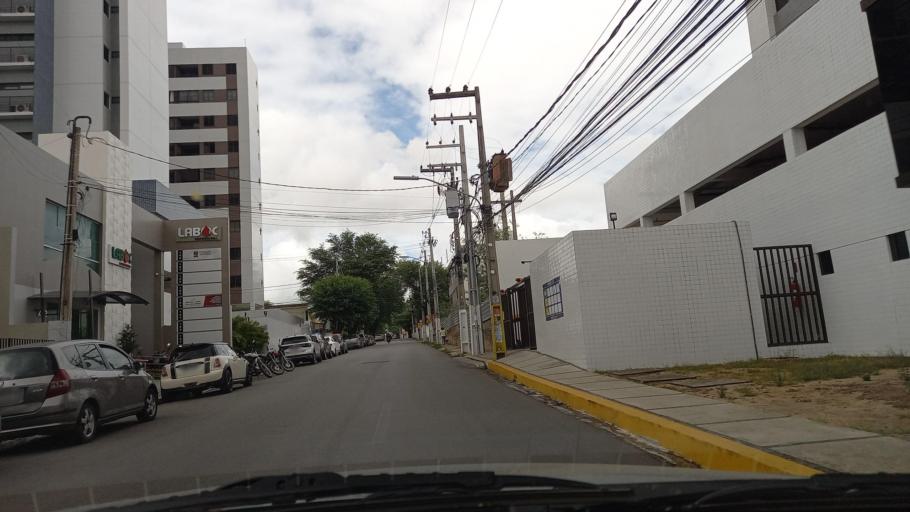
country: BR
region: Pernambuco
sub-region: Caruaru
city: Caruaru
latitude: -8.2798
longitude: -35.9676
